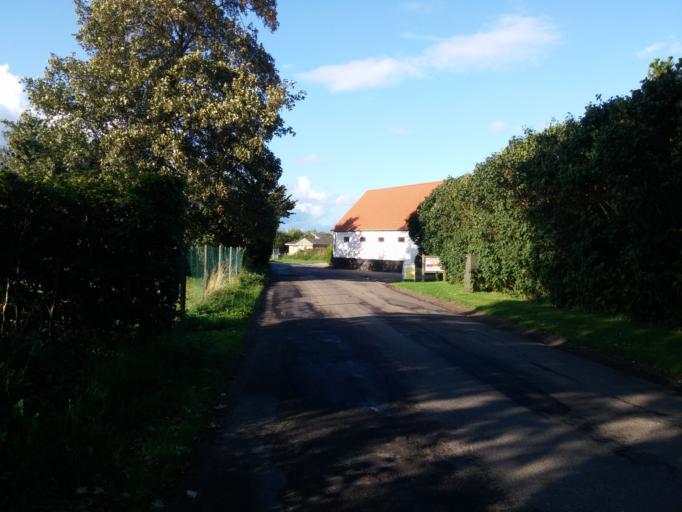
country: DK
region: Zealand
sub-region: Kalundborg Kommune
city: Svebolle
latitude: 55.7502
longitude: 11.3383
